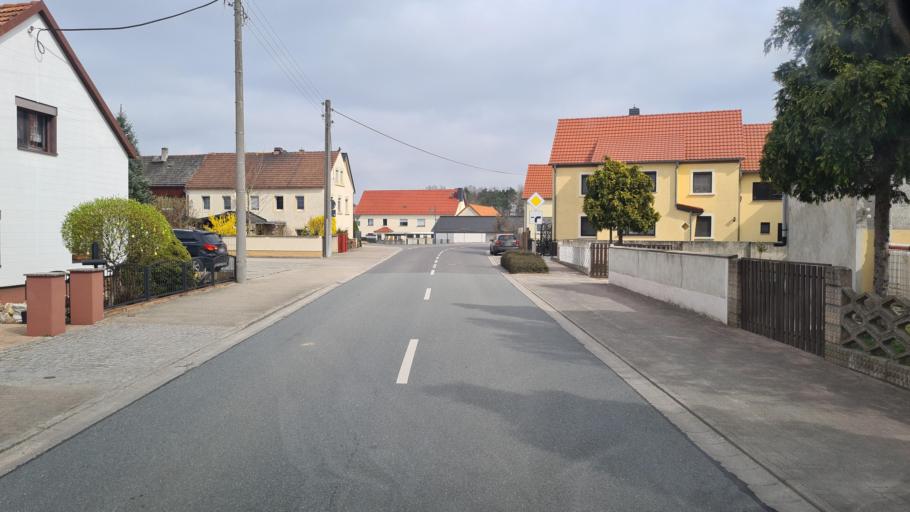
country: DE
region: Saxony
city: Zabeltitz
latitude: 51.3894
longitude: 13.4809
